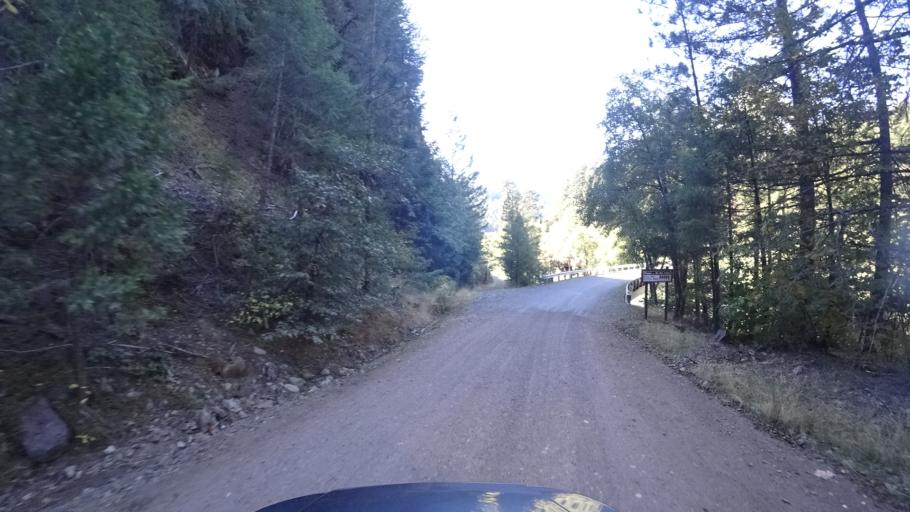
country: US
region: California
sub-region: Siskiyou County
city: Happy Camp
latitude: 41.2976
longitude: -123.1251
